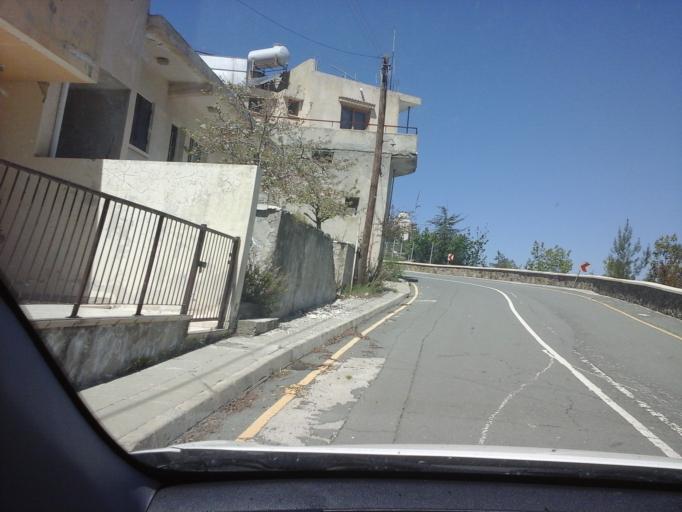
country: CY
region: Lefkosia
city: Kakopetria
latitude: 35.0016
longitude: 32.8023
